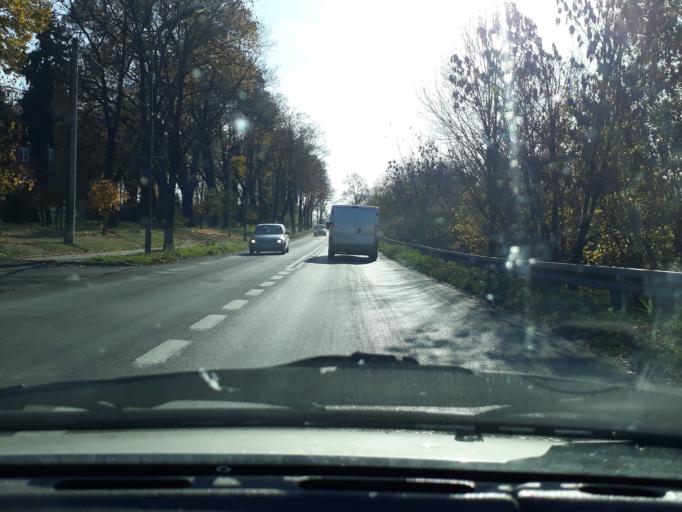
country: PL
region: Silesian Voivodeship
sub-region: Powiat tarnogorski
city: Tarnowskie Gory
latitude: 50.4391
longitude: 18.8618
